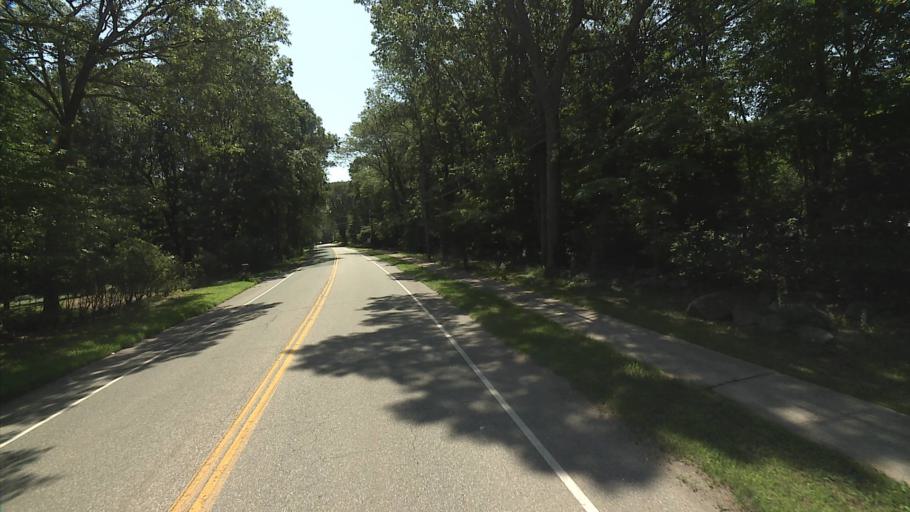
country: US
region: Connecticut
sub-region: Middlesex County
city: Westbrook Center
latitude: 41.2945
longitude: -72.4334
